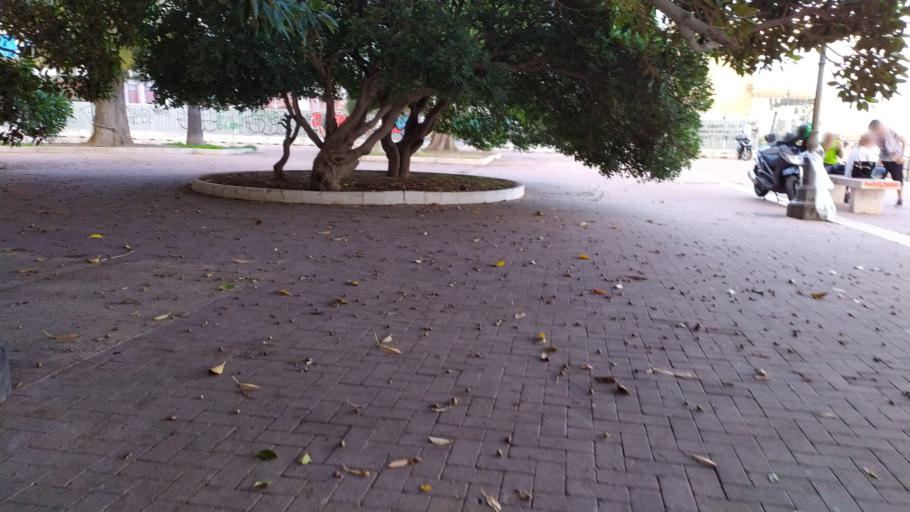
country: IT
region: Sicily
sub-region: Messina
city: Messina
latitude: 38.2015
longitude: 15.5601
